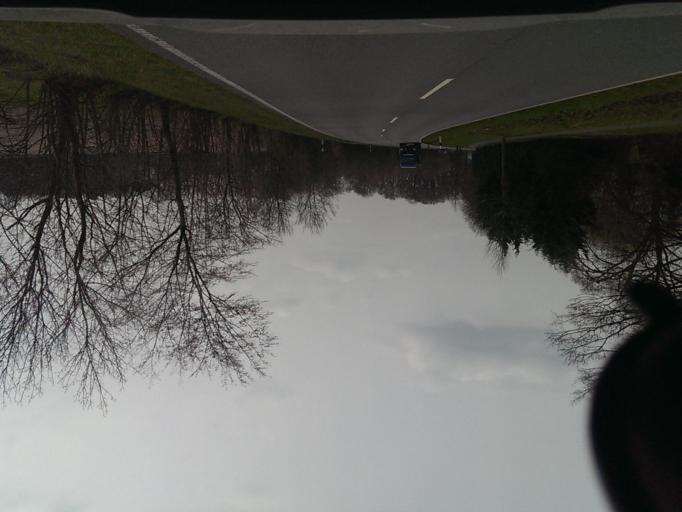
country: DE
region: North Rhine-Westphalia
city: Rietberg
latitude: 51.7569
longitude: 8.4807
